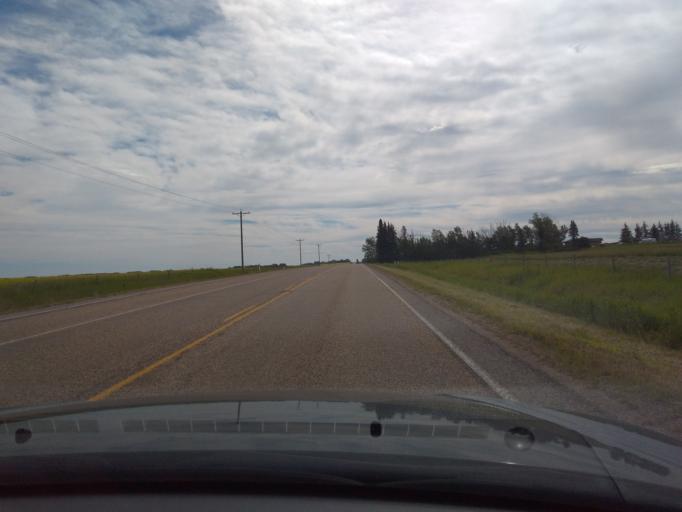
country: CA
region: Alberta
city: Carstairs
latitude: 51.5329
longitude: -114.1984
